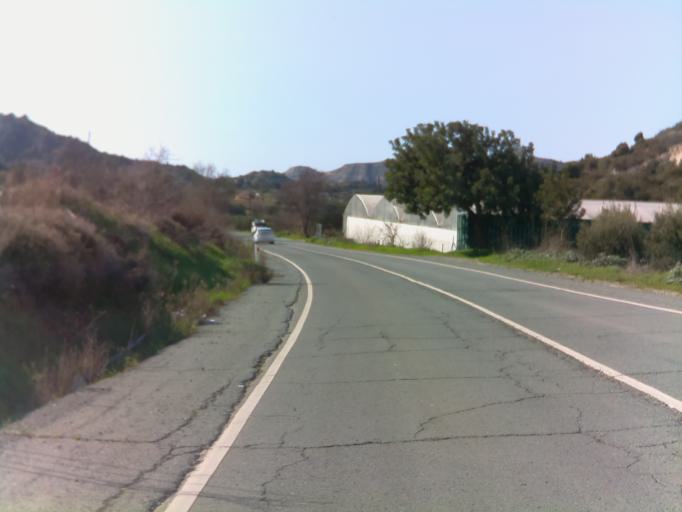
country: CY
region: Limassol
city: Pissouri
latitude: 34.6734
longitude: 32.6889
